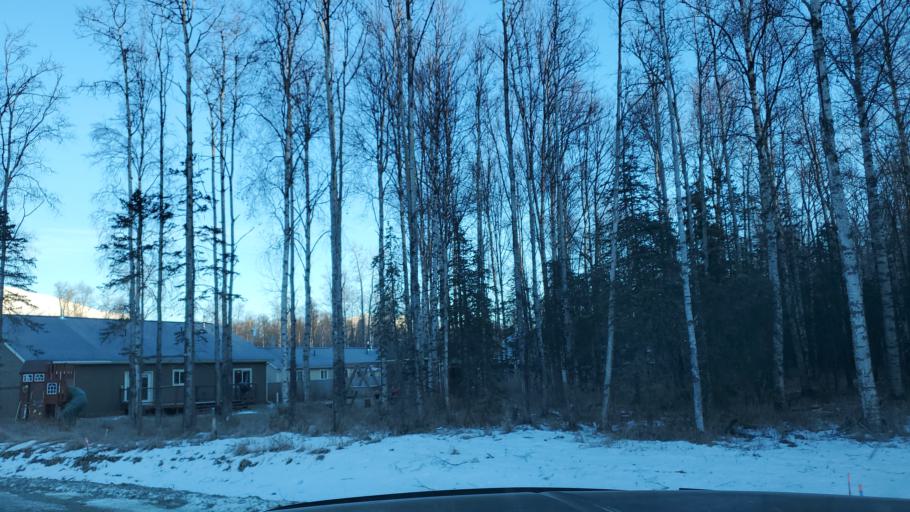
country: US
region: Alaska
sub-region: Matanuska-Susitna Borough
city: Lakes
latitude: 61.6550
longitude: -149.3401
